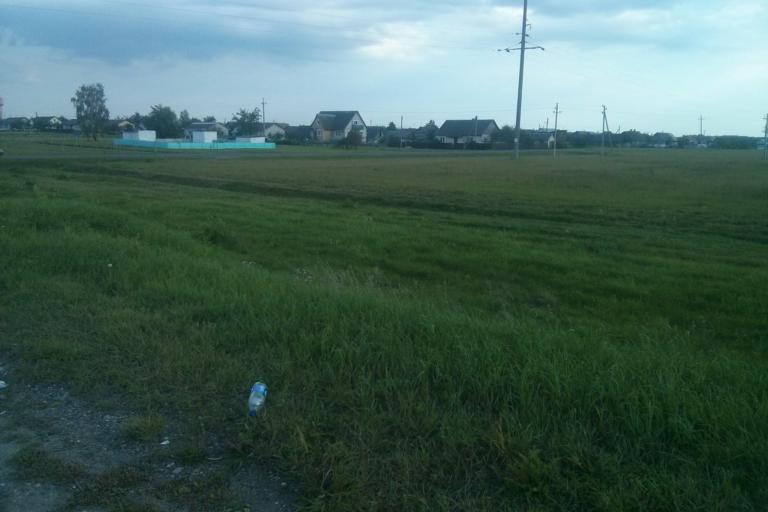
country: BY
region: Minsk
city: Chervyen'
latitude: 53.7230
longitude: 28.3832
